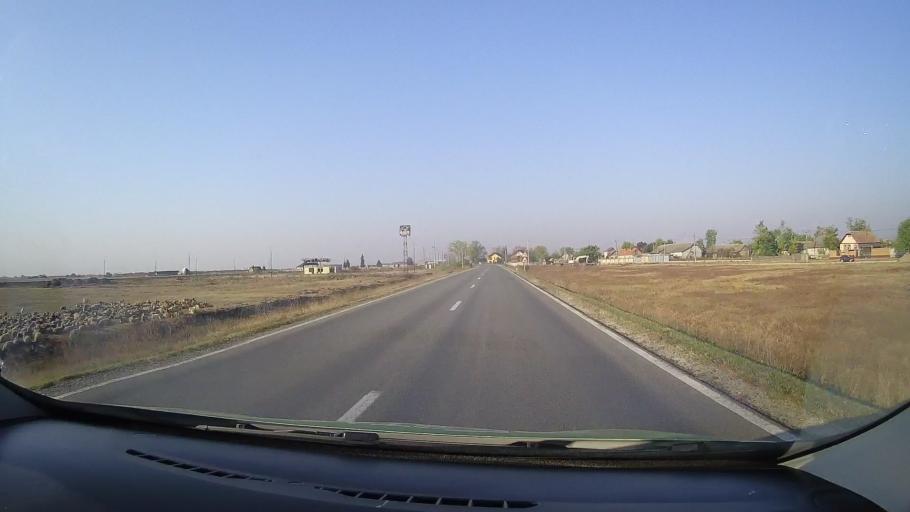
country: RO
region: Arad
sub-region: Comuna Socodor
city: Socodor
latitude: 46.5027
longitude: 21.4475
